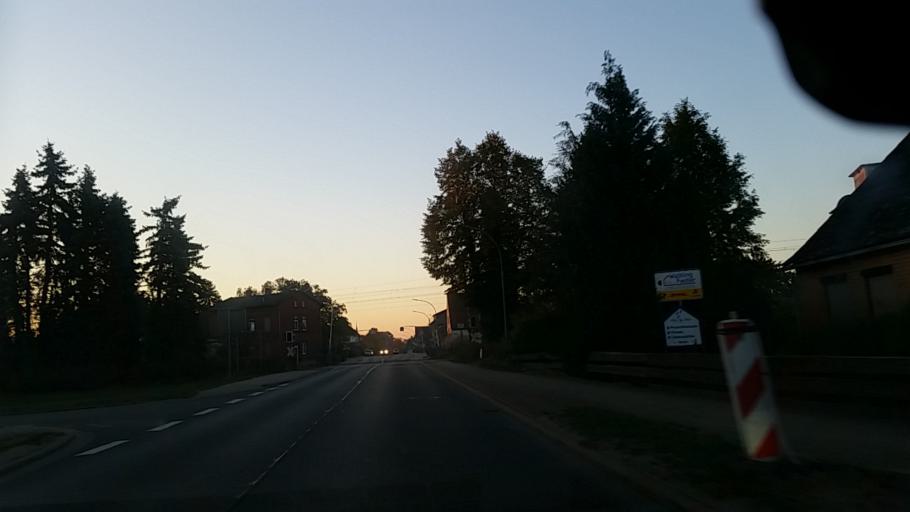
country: DE
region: Lower Saxony
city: Wieren
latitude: 52.8933
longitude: 10.6531
